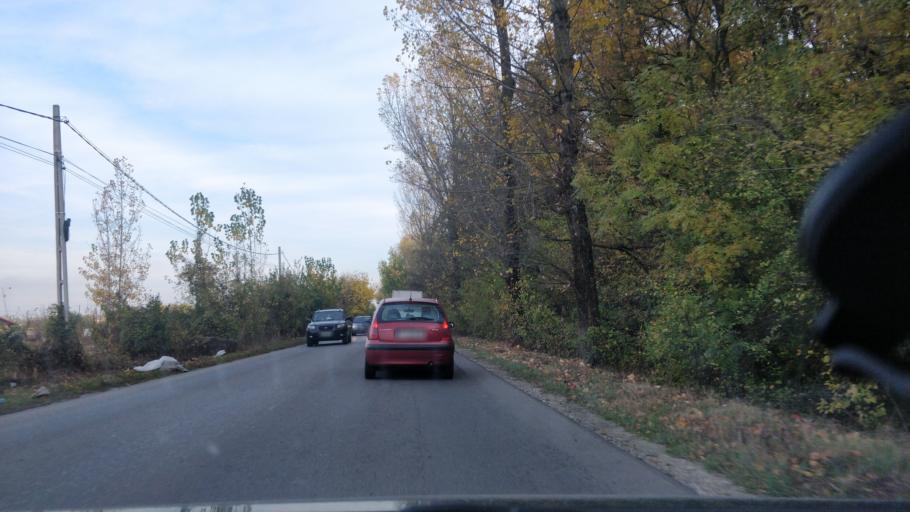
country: RO
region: Giurgiu
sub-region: Comuna Bolintin Deal
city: Bolintin Deal
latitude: 44.4476
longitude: 25.8497
